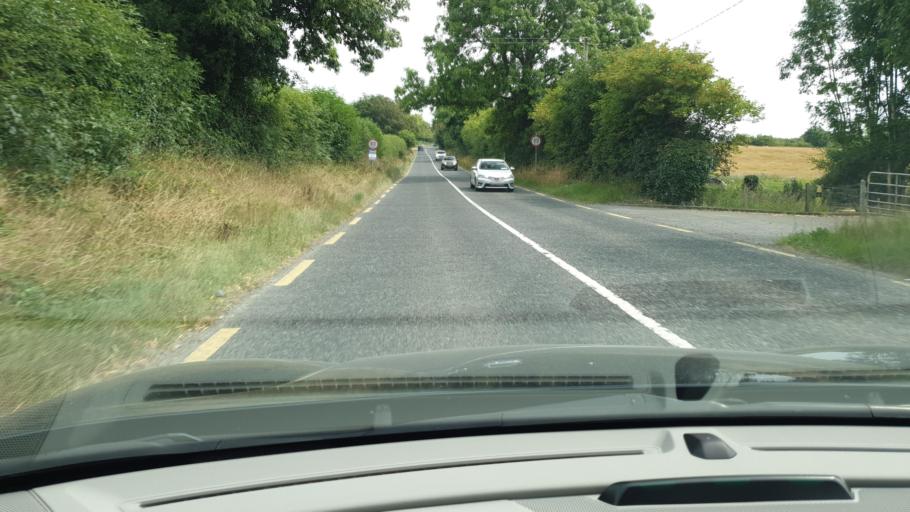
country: IE
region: Leinster
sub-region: An Mhi
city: Navan
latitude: 53.6462
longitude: -6.6412
